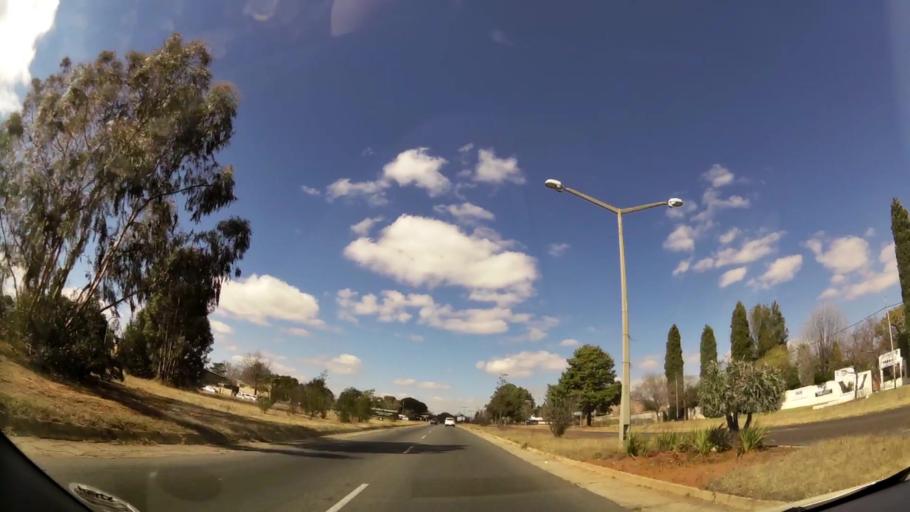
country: ZA
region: Gauteng
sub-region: West Rand District Municipality
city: Krugersdorp
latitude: -26.0945
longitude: 27.7907
